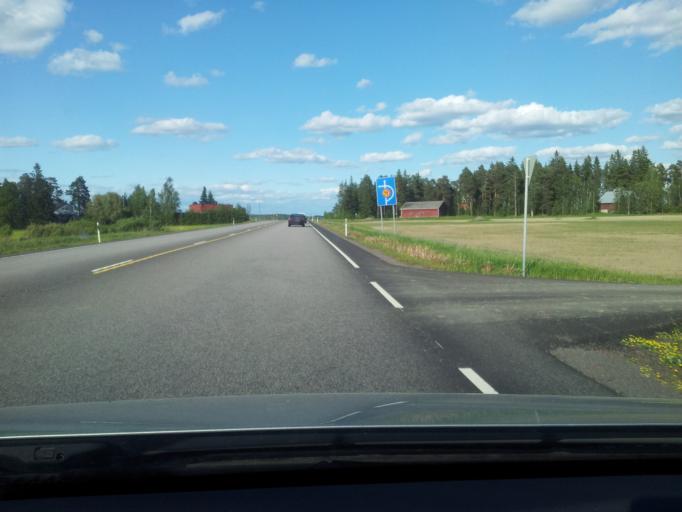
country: FI
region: Uusimaa
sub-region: Loviisa
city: Lapinjaervi
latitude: 60.6946
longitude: 26.2909
